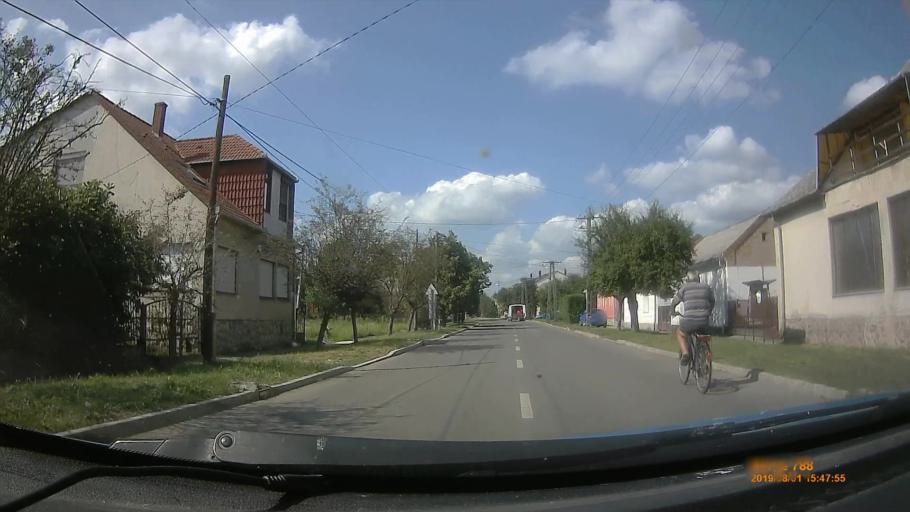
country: HU
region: Baranya
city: Szentlorinc
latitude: 46.0345
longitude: 17.9849
